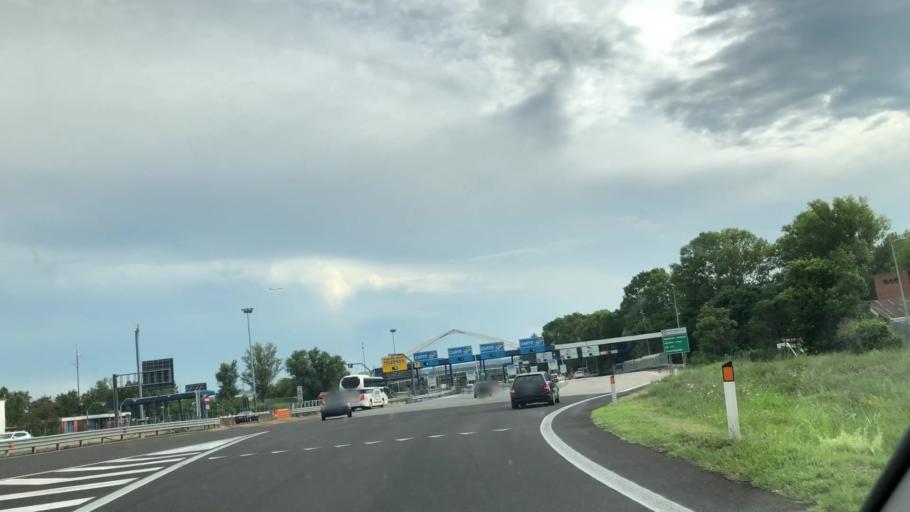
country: IT
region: Emilia-Romagna
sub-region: Provincia di Bologna
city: Progresso
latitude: 44.5317
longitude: 11.3605
